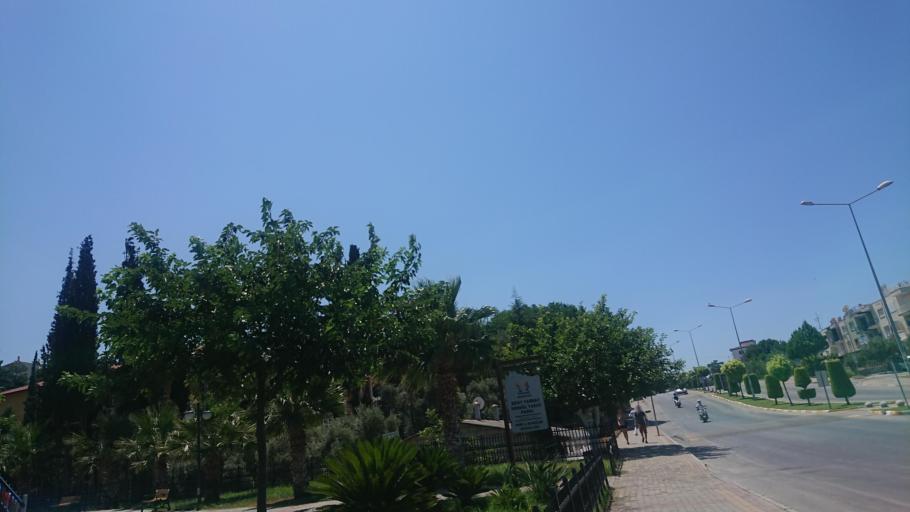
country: TR
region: Aydin
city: Kusadasi
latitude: 37.8683
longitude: 27.2683
